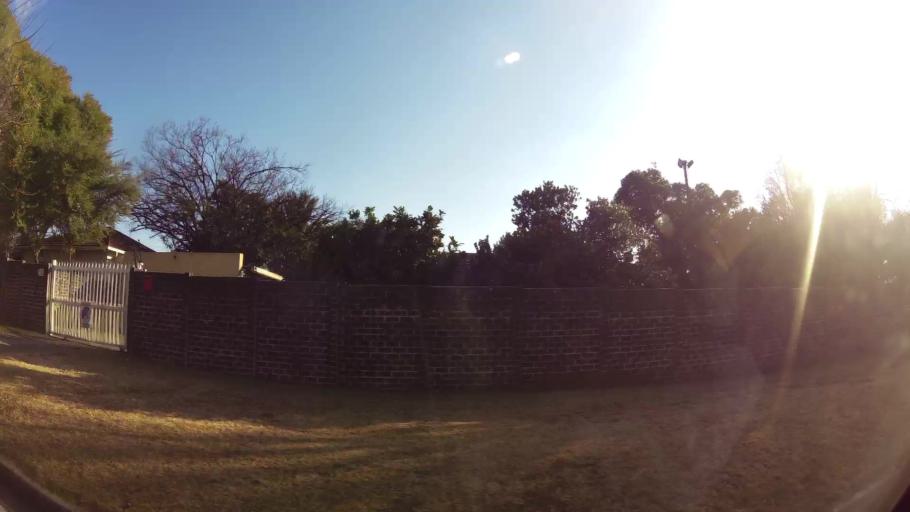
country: ZA
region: Gauteng
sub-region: Ekurhuleni Metropolitan Municipality
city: Germiston
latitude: -26.2005
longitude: 28.1309
